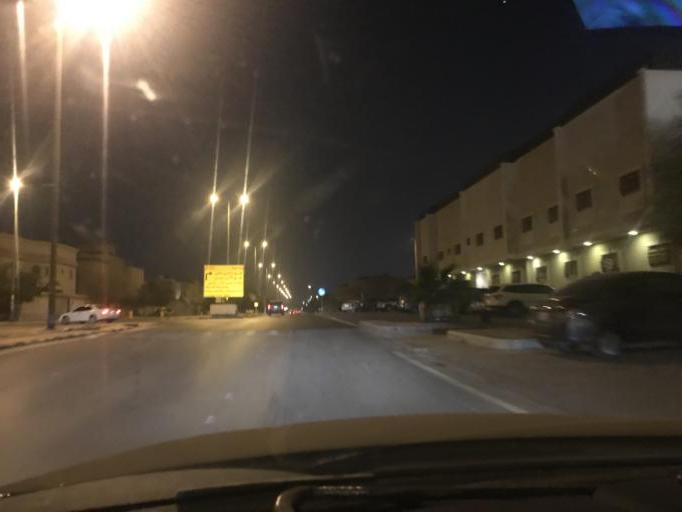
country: SA
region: Ar Riyad
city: Riyadh
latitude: 24.6770
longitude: 46.7857
